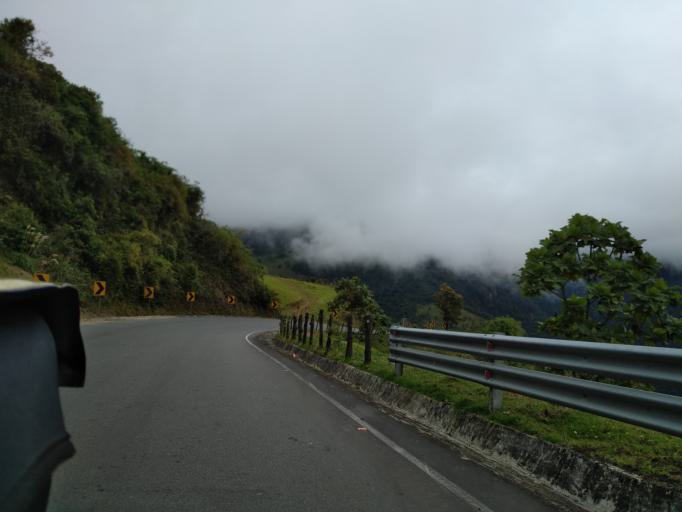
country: EC
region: Cotopaxi
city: La Mana
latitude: -0.9659
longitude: -78.9888
